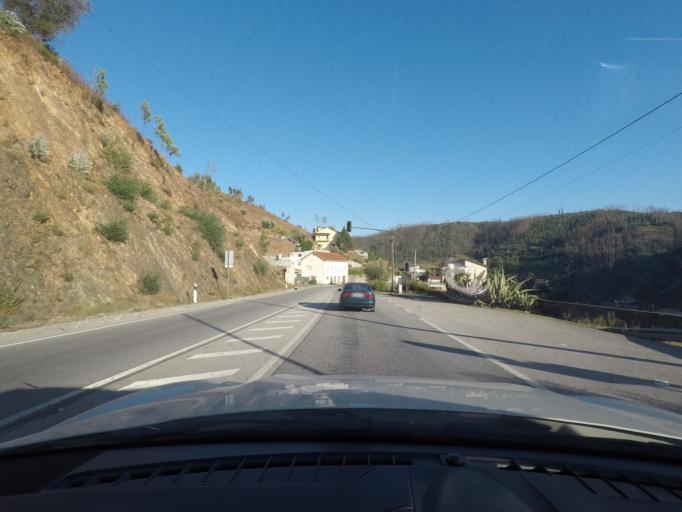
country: PT
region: Coimbra
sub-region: Vila Nova de Poiares
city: Poiares
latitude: 40.1726
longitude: -8.3218
